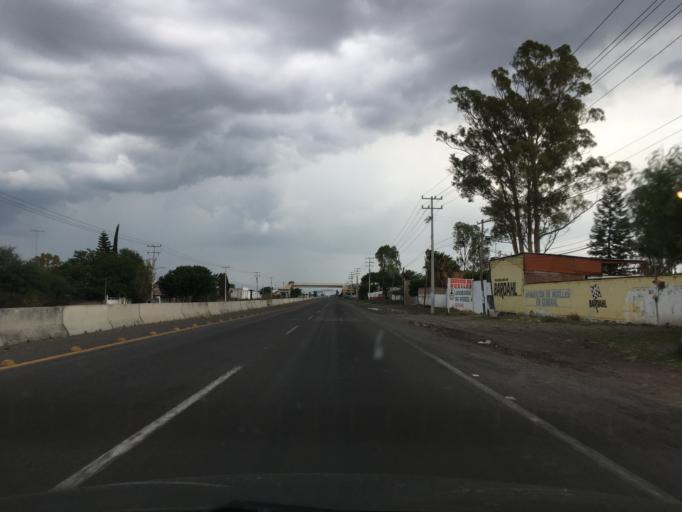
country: MX
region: Guanajuato
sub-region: Celaya
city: El Sauz (El Sauz de Villasenor)
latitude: 20.3903
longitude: -100.7912
